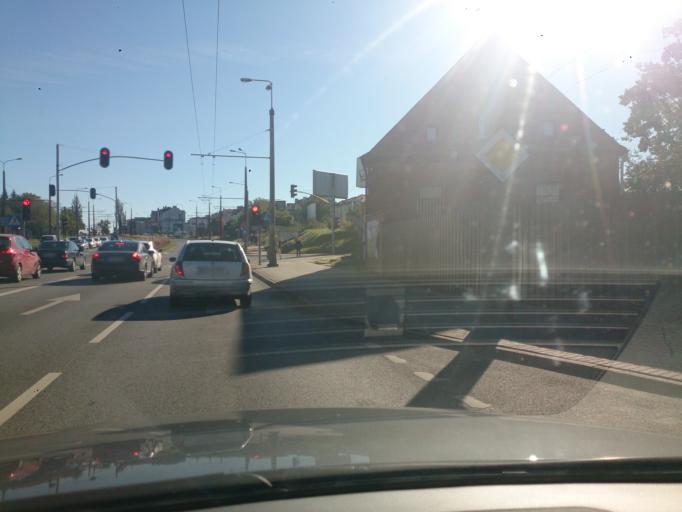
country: PL
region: Pomeranian Voivodeship
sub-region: Gdynia
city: Wielki Kack
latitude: 54.4702
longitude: 18.4958
